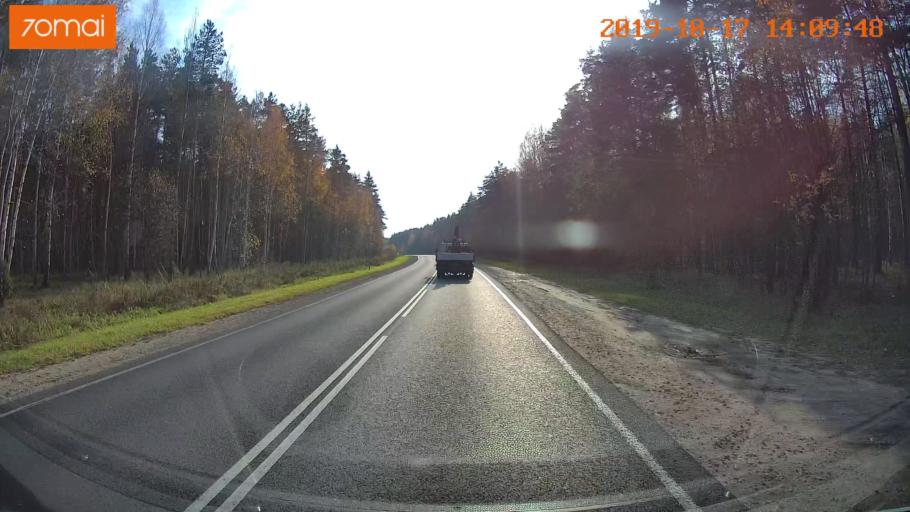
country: RU
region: Rjazan
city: Spas-Klepiki
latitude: 55.0854
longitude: 40.0546
